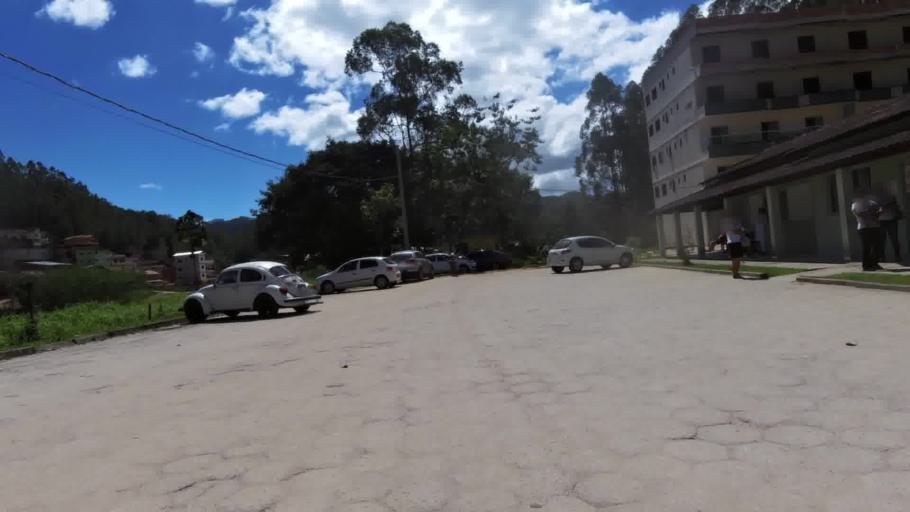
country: BR
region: Espirito Santo
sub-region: Vargem Alta
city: Vargem Alta
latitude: -20.6723
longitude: -41.0064
